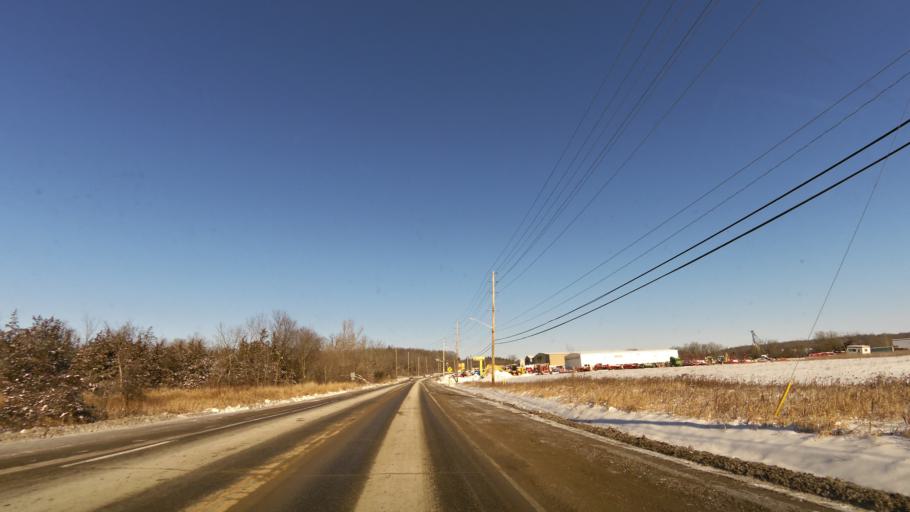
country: CA
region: Ontario
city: Quinte West
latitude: 44.2835
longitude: -77.8093
